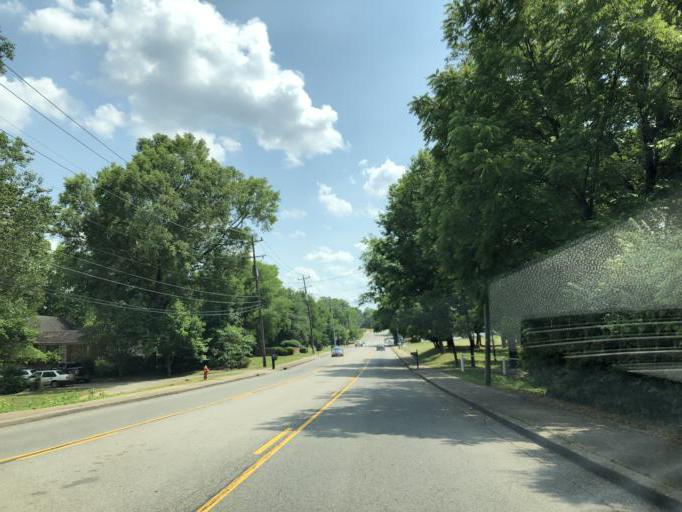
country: US
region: Tennessee
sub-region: Davidson County
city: Goodlettsville
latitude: 36.2512
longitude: -86.7342
